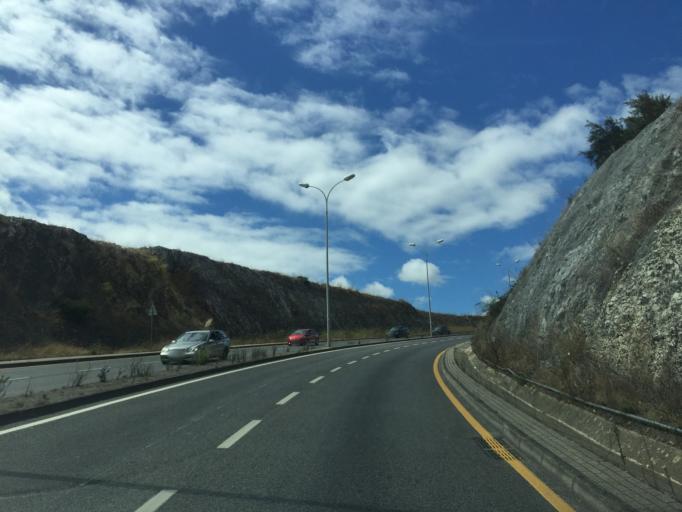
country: PT
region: Lisbon
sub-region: Odivelas
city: Famoes
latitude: 38.7724
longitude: -9.2225
